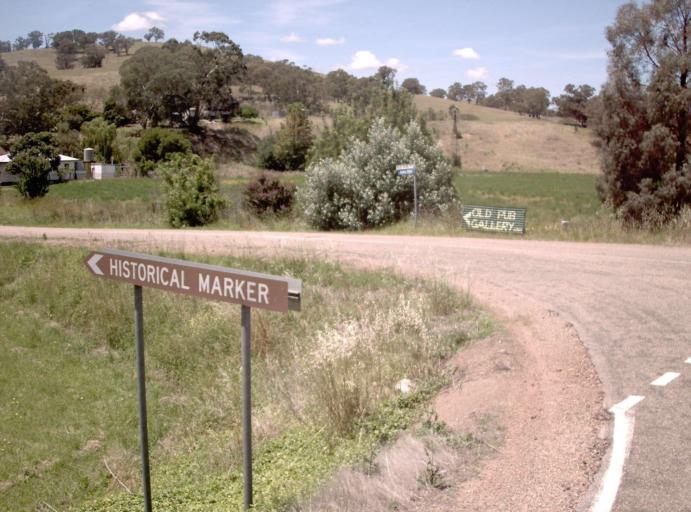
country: AU
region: Victoria
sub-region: East Gippsland
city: Bairnsdale
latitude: -37.3810
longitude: 147.8304
